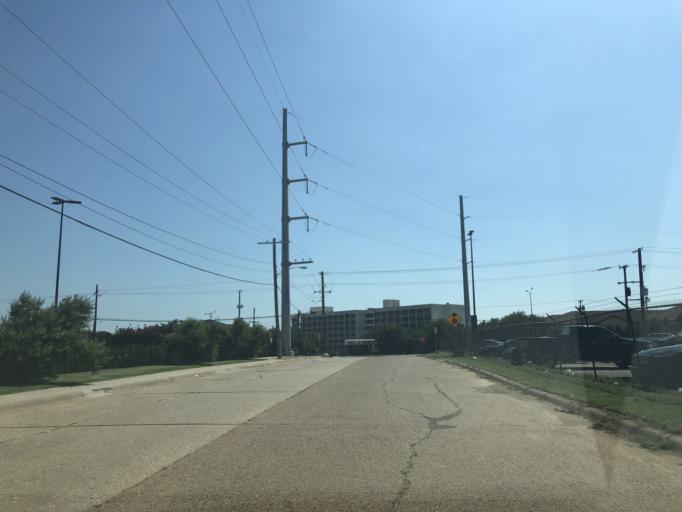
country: US
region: Texas
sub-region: Dallas County
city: University Park
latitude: 32.8249
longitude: -96.8515
